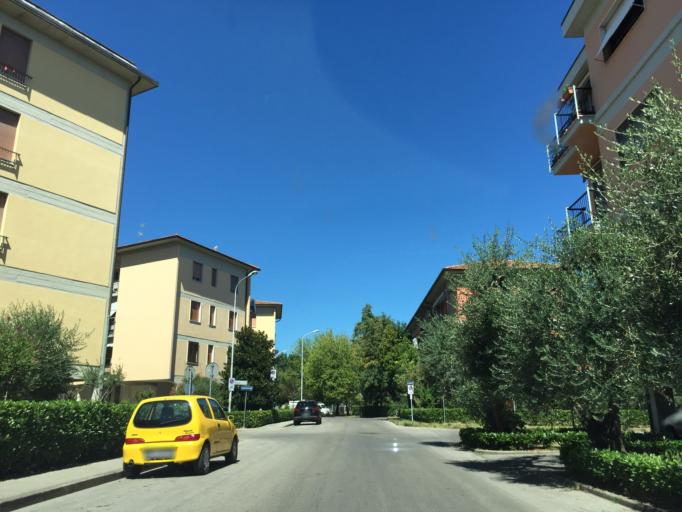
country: IT
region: Tuscany
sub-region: Provincia di Pistoia
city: Pistoia
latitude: 43.9517
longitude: 10.9047
